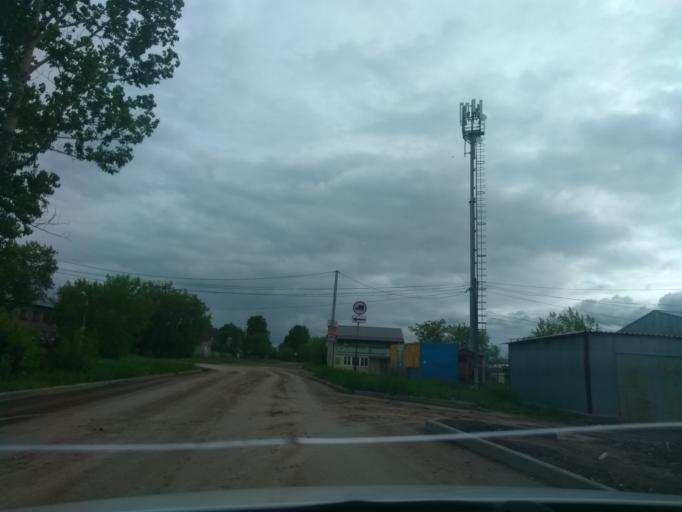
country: RU
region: Perm
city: Froly
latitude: 57.9216
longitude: 56.2690
